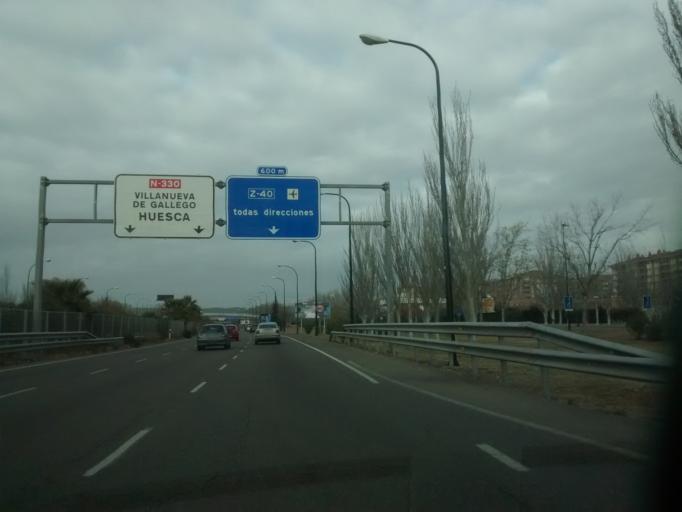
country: ES
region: Aragon
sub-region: Provincia de Zaragoza
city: Zaragoza
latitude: 41.6679
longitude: -0.8800
